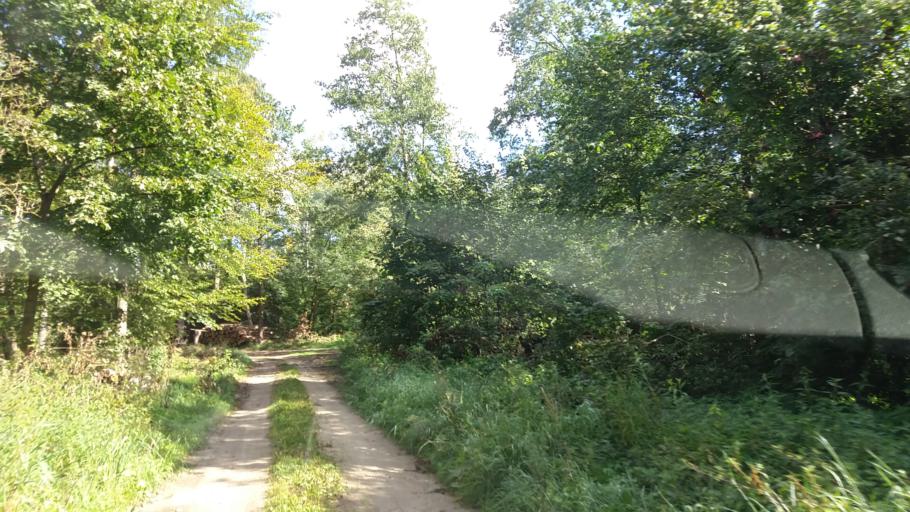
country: PL
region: West Pomeranian Voivodeship
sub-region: Powiat choszczenski
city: Krzecin
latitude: 53.1414
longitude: 15.4819
